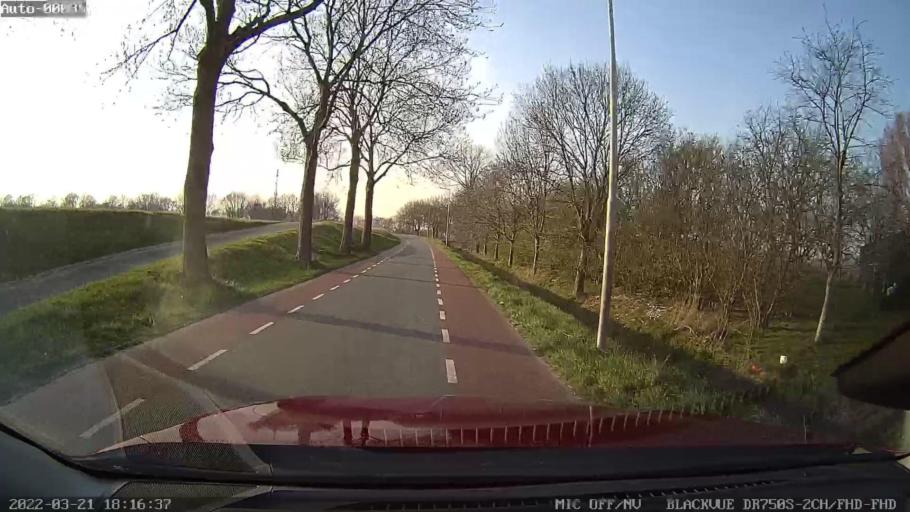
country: NL
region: North Brabant
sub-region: Gemeente Steenbergen
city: Nieuw-Vossemeer
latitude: 51.5804
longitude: 4.2239
